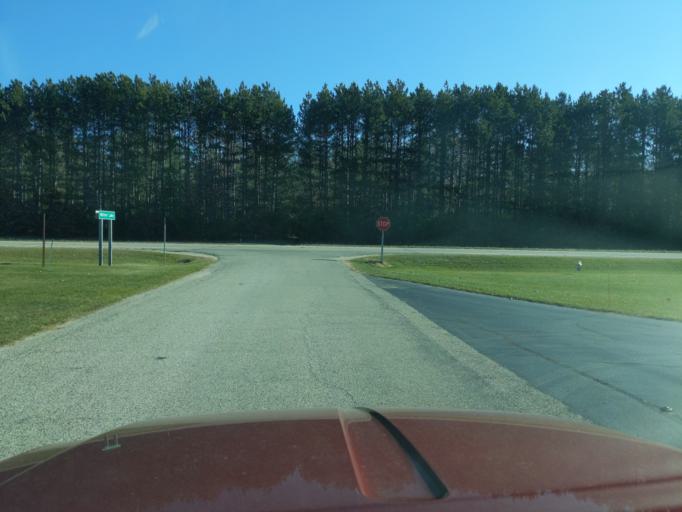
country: US
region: Wisconsin
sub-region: Waushara County
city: Wautoma
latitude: 44.0332
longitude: -89.2985
